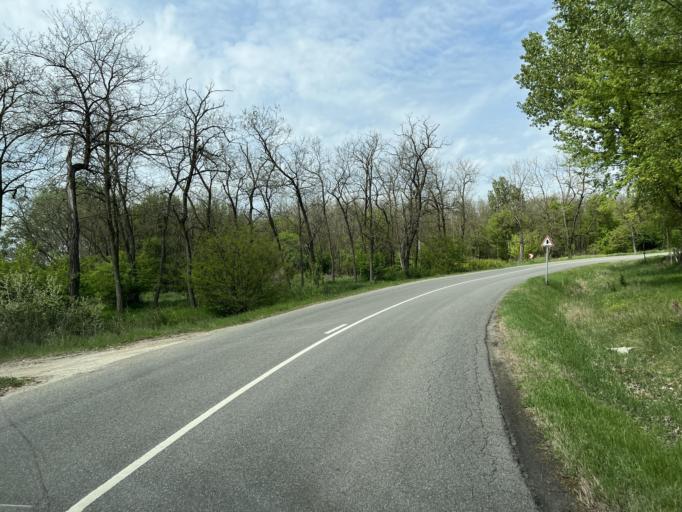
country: HU
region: Pest
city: Albertirsa
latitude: 47.1579
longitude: 19.6114
